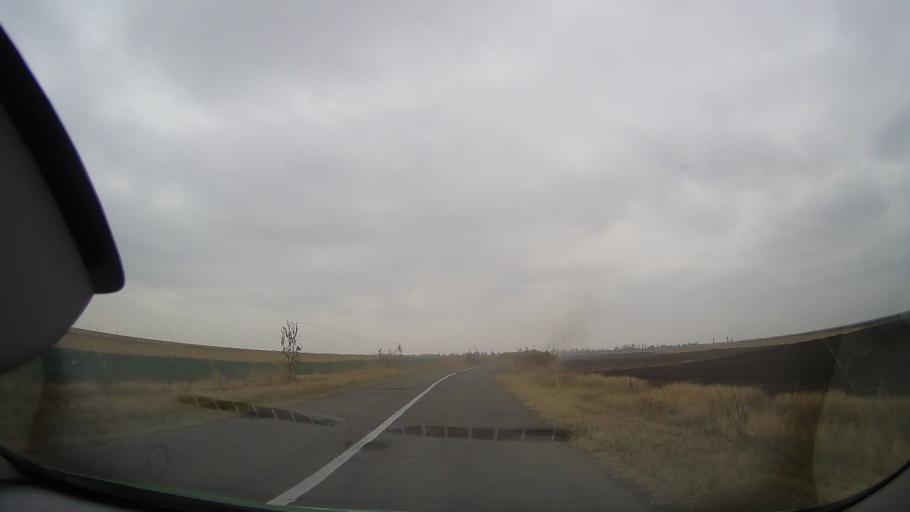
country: RO
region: Ialomita
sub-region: Comuna Valea Macrisului
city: Valea Macrisului
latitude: 44.7613
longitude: 26.7987
